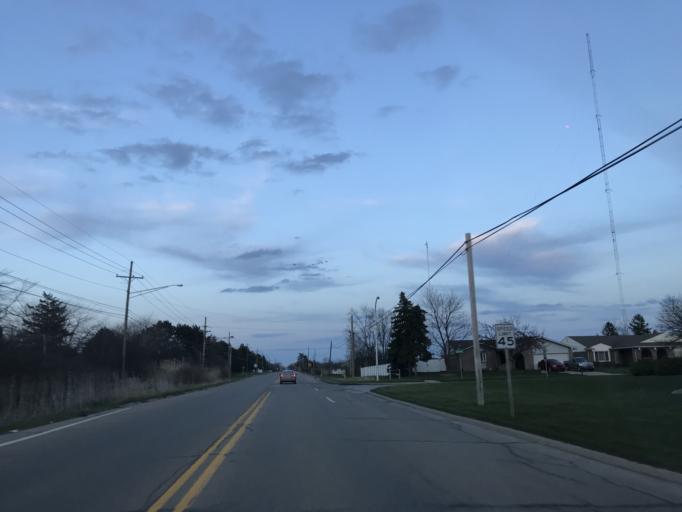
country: US
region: Michigan
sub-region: Wayne County
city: Woodhaven
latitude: 42.1697
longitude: -83.2191
